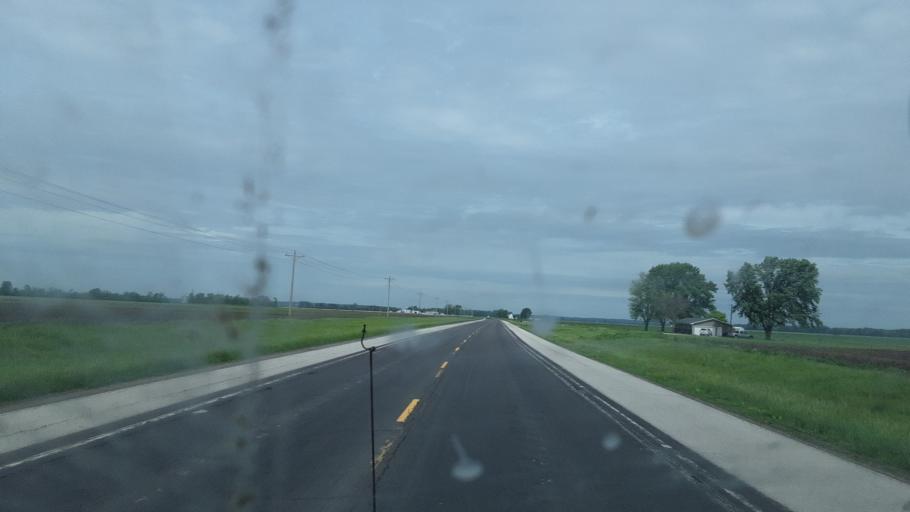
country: US
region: Illinois
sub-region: Hancock County
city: Warsaw
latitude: 40.3775
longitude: -91.4917
